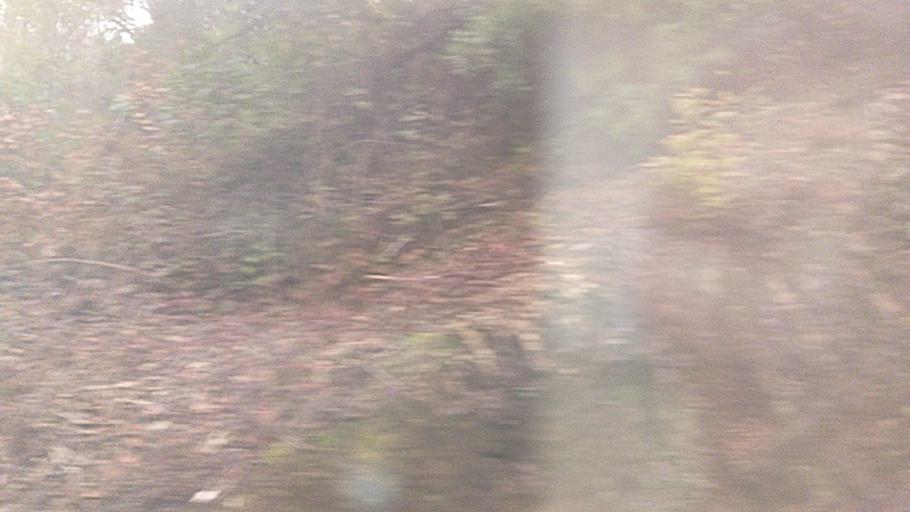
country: PT
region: Viseu
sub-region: Mortagua
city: Mortagua
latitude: 40.4129
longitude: -8.3093
